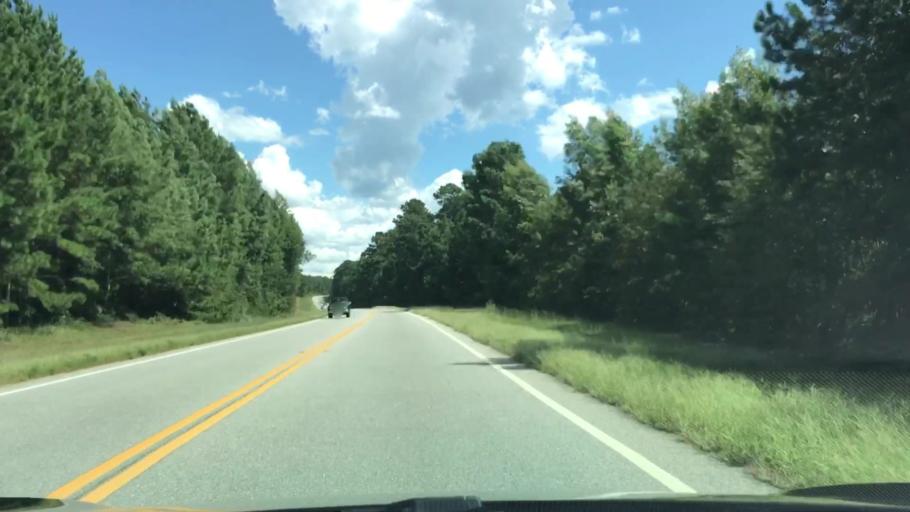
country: US
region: Georgia
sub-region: Greene County
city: Greensboro
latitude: 33.6666
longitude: -83.2544
